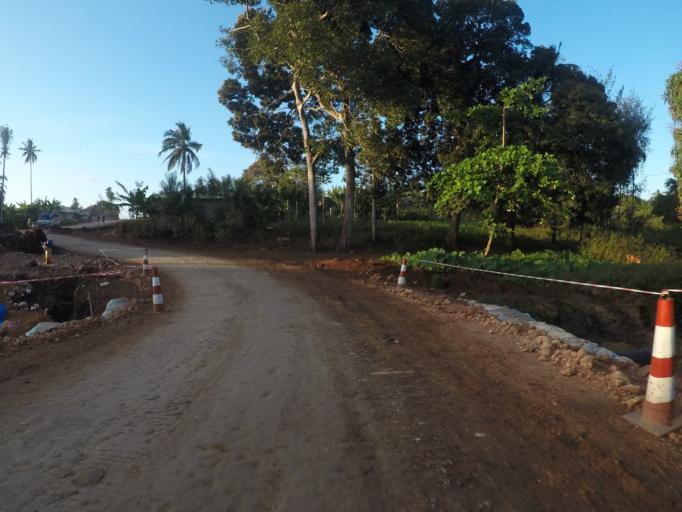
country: TZ
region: Zanzibar North
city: Gamba
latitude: -5.9152
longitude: 39.2994
